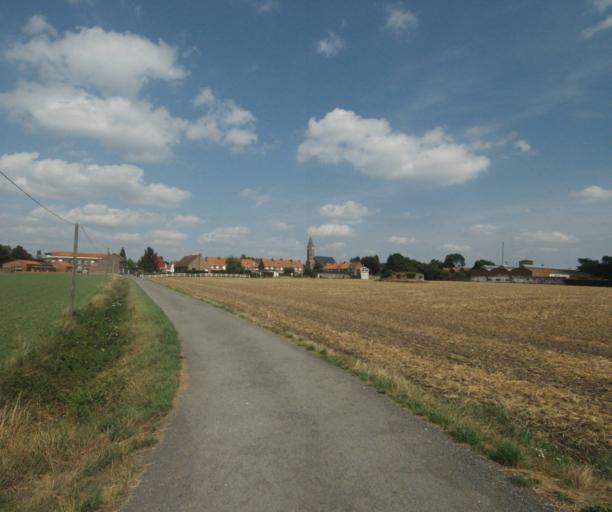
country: FR
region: Nord-Pas-de-Calais
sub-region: Departement du Nord
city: Hem
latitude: 50.6490
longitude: 3.1868
